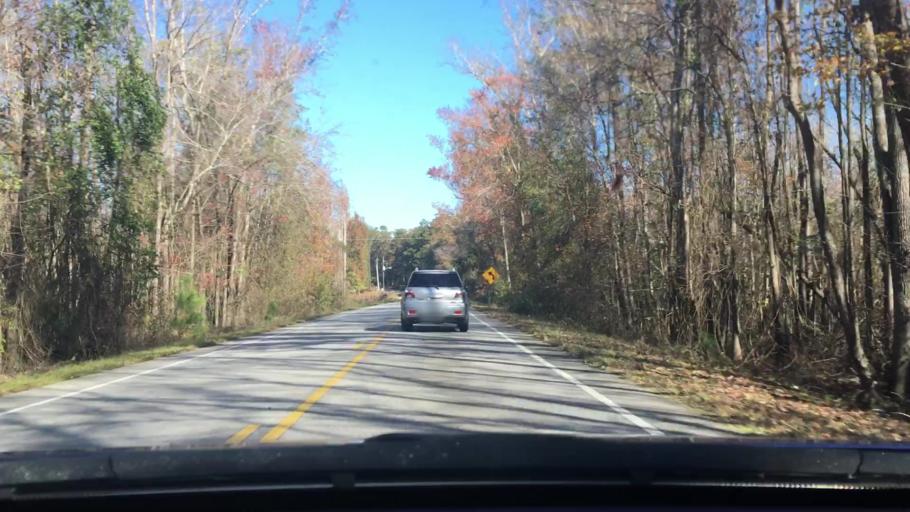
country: US
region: South Carolina
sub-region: Sumter County
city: South Sumter
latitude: 33.8813
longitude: -80.3648
